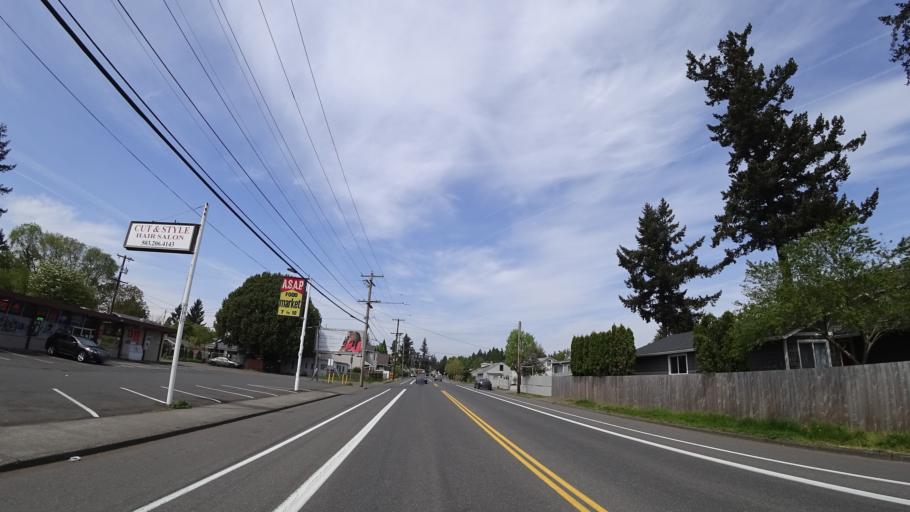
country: US
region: Oregon
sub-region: Clackamas County
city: Milwaukie
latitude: 45.4694
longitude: -122.6100
